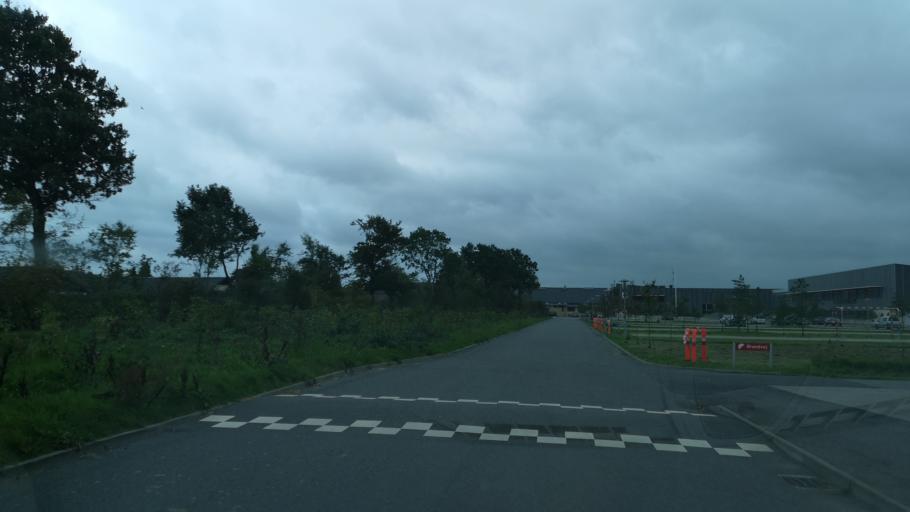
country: DK
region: Central Jutland
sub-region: Herning Kommune
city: Snejbjerg
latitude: 56.1302
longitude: 8.8867
